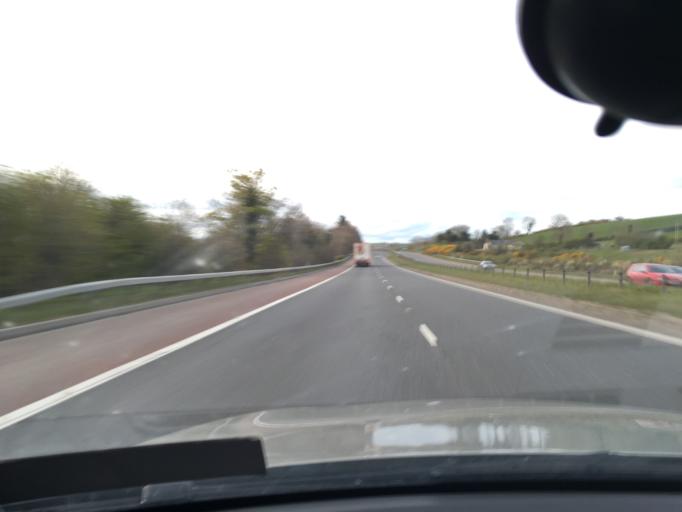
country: GB
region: Northern Ireland
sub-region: Banbridge District
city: Banbridge
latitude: 54.2663
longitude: -6.3135
